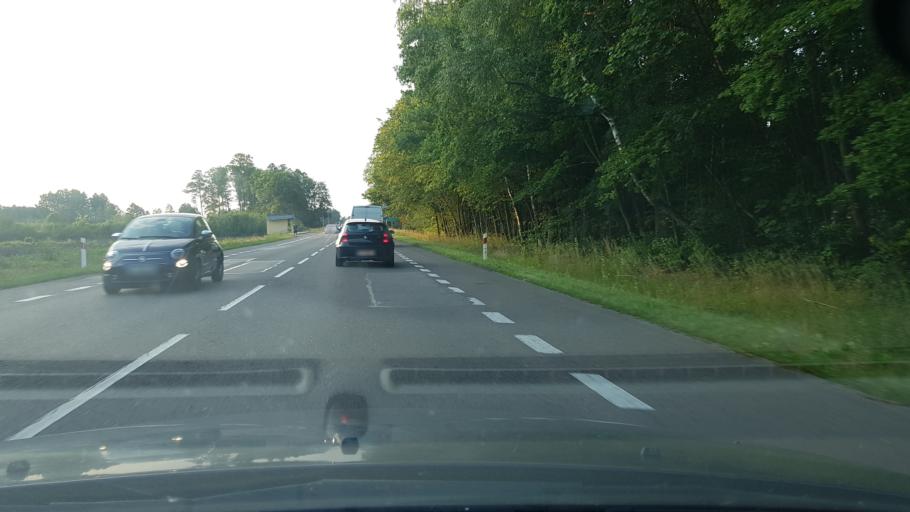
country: PL
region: Masovian Voivodeship
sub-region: Powiat ciechanowski
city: Glinojeck
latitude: 52.7496
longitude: 20.3149
